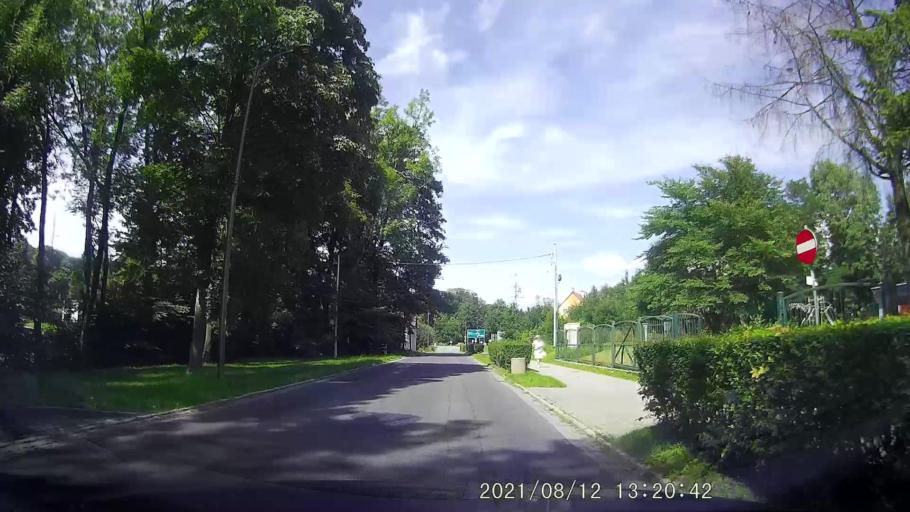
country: PL
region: Lower Silesian Voivodeship
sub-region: Powiat klodzki
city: Stronie Slaskie
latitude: 50.2895
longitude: 16.8761
